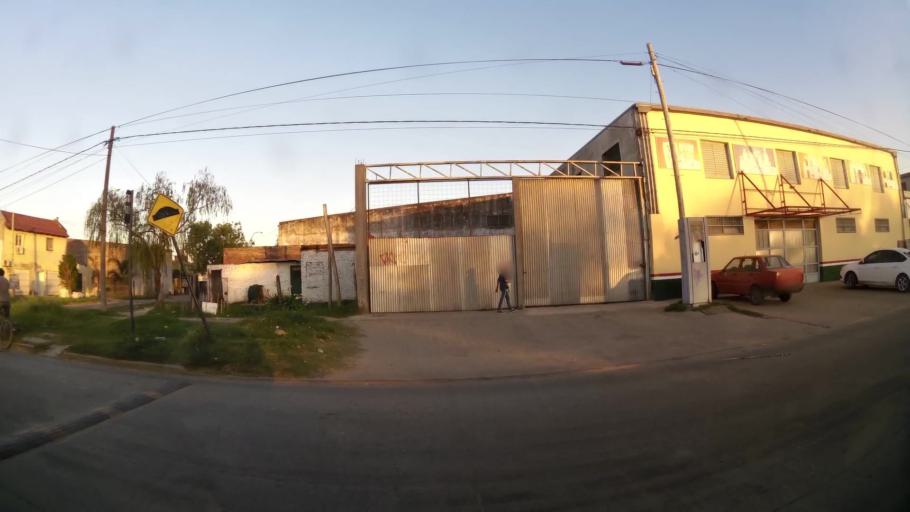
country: AR
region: Santa Fe
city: Santa Fe de la Vera Cruz
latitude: -31.5975
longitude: -60.7006
